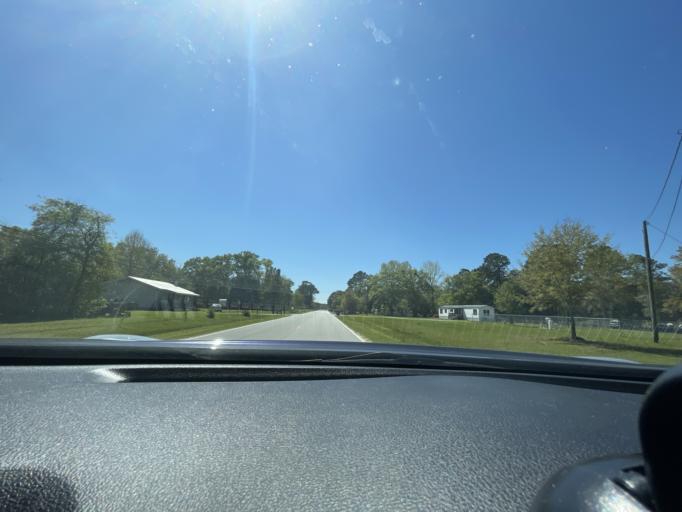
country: US
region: Georgia
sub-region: Chatham County
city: Bloomingdale
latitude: 32.0968
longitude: -81.2941
